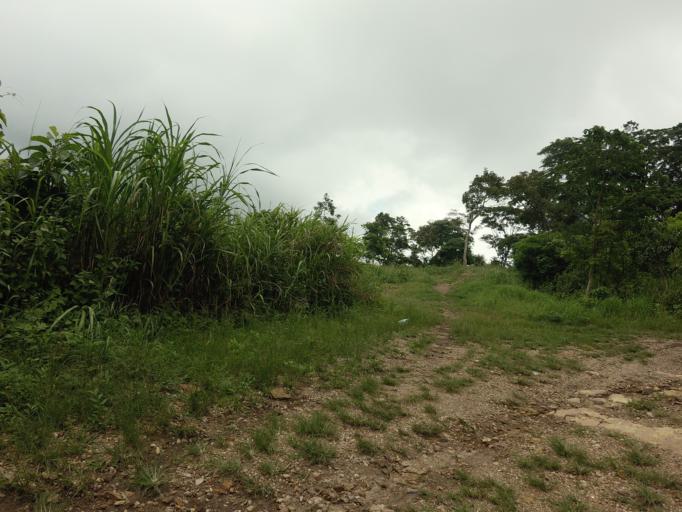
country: TG
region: Plateaux
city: Kpalime
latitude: 6.8454
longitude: 0.4419
